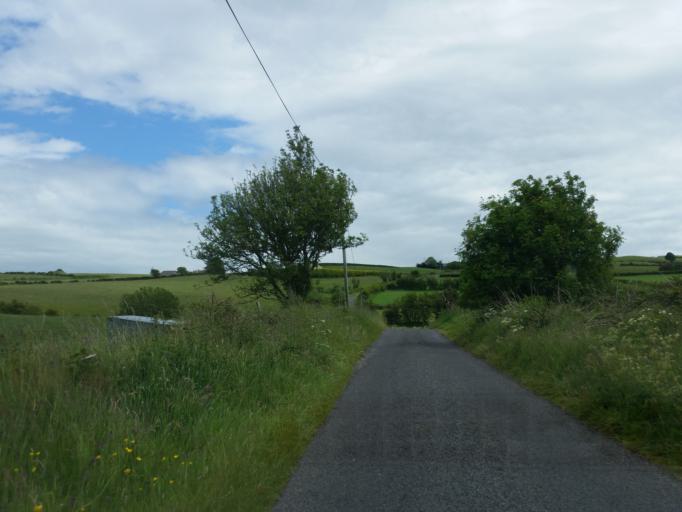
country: GB
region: Northern Ireland
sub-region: Omagh District
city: Omagh
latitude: 54.5583
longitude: -7.0659
